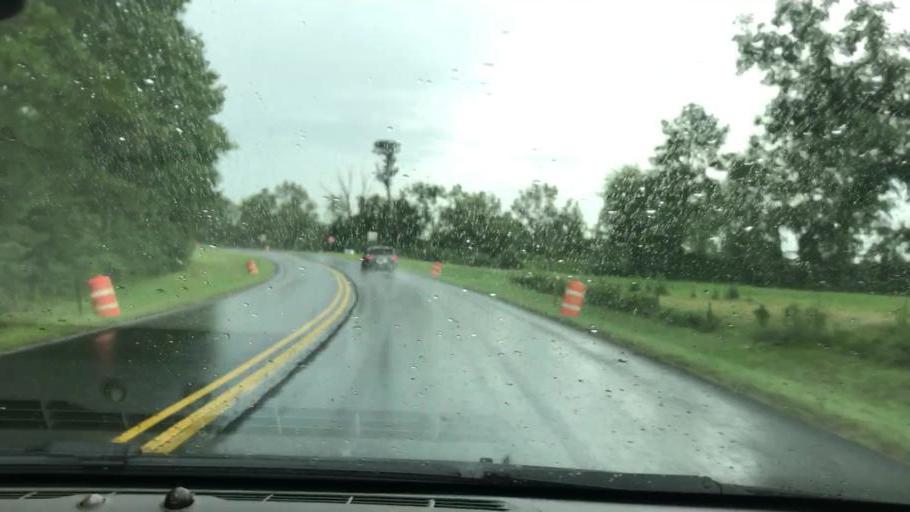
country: US
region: Georgia
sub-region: Clay County
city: Fort Gaines
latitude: 31.5735
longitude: -85.0196
